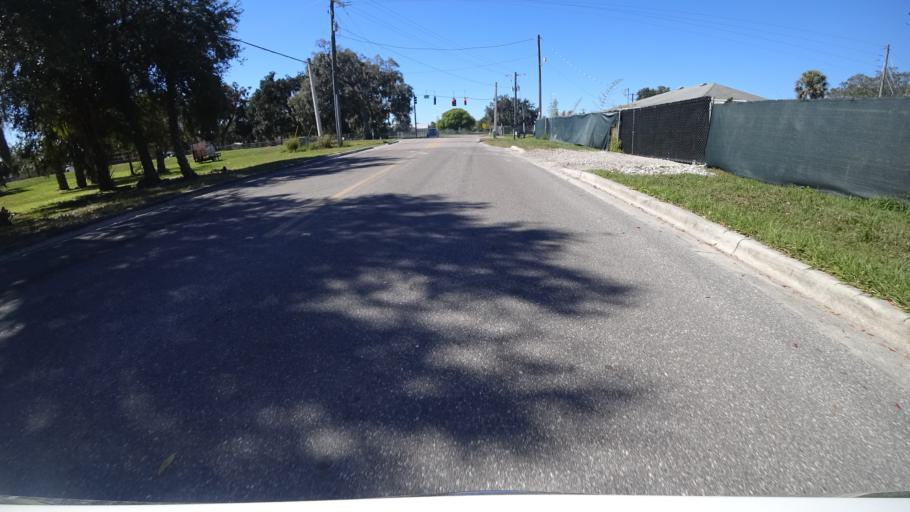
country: US
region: Florida
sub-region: Manatee County
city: Memphis
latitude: 27.5394
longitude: -82.5478
